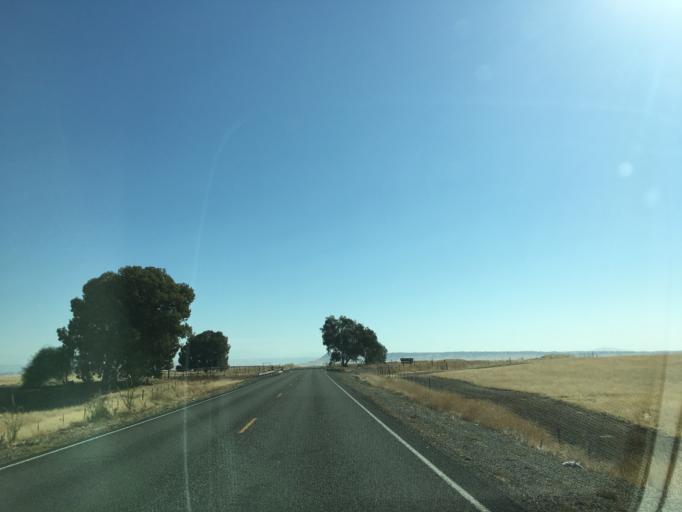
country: US
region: California
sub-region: Madera County
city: Bonadelle Ranchos-Madera Ranchos
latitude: 37.0103
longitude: -119.8431
